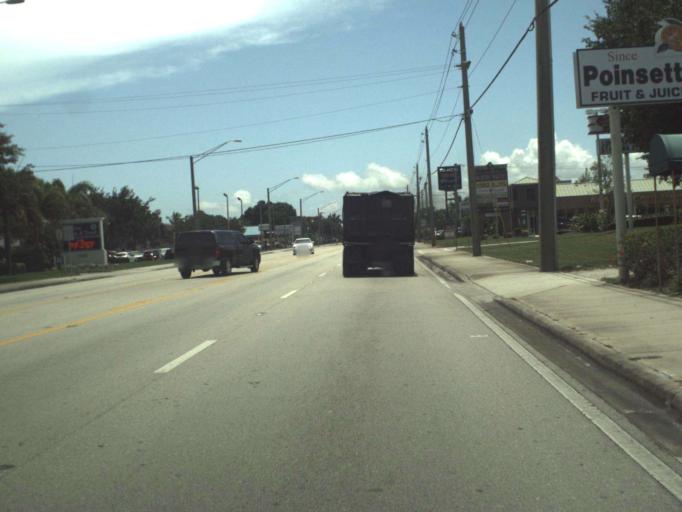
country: US
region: Florida
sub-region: Indian River County
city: Vero Beach
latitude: 27.6289
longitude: -80.3893
